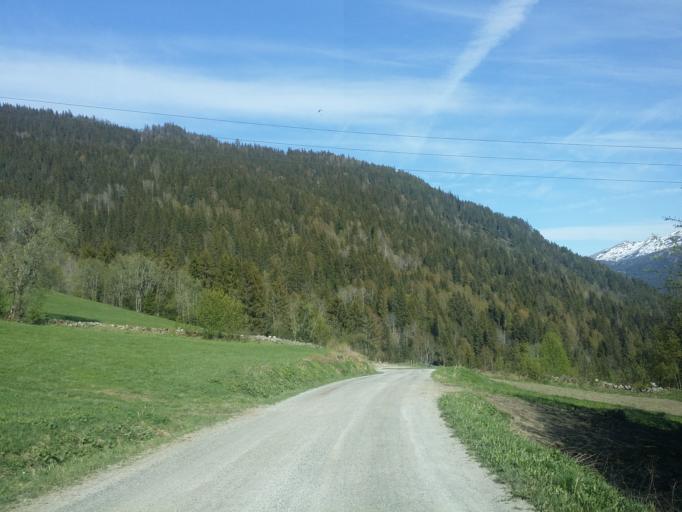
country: NO
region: Telemark
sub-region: Seljord
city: Seljord
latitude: 59.6153
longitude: 8.6914
